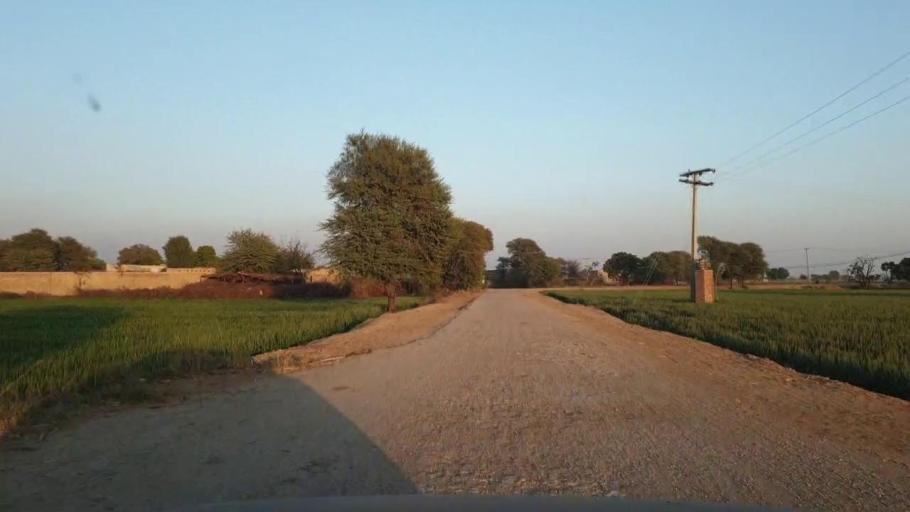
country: PK
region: Sindh
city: Tando Jam
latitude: 25.3127
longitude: 68.6386
